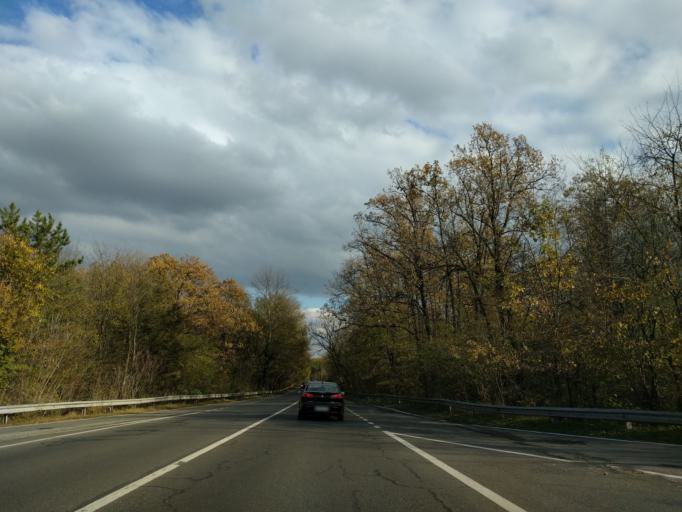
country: RO
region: Ilfov
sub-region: Comuna Branesti
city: Branesti
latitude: 44.4615
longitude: 26.3179
